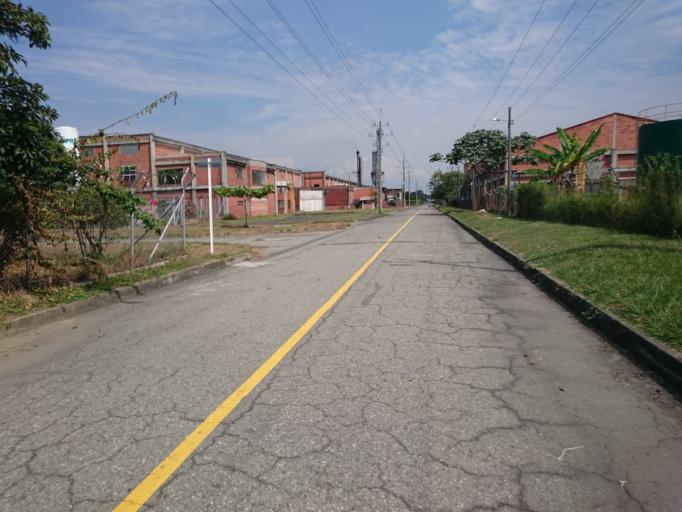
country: CO
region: Cauca
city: Puerto Tejada
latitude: 3.2019
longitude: -76.4154
